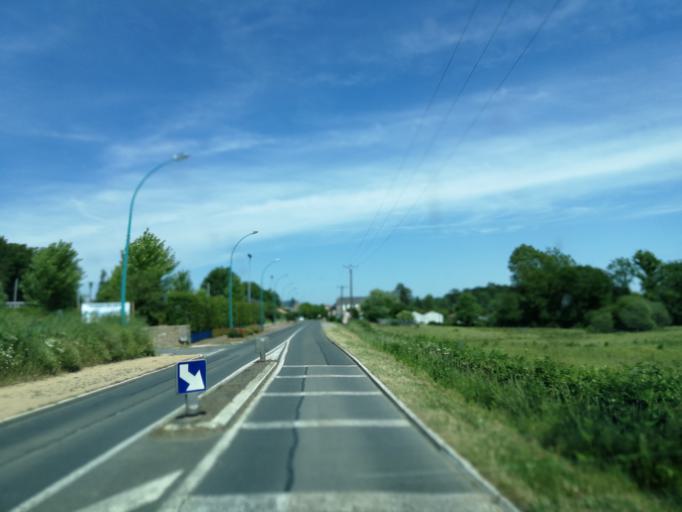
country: FR
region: Poitou-Charentes
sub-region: Departement des Deux-Sevres
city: Courlay
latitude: 46.8086
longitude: -0.5641
